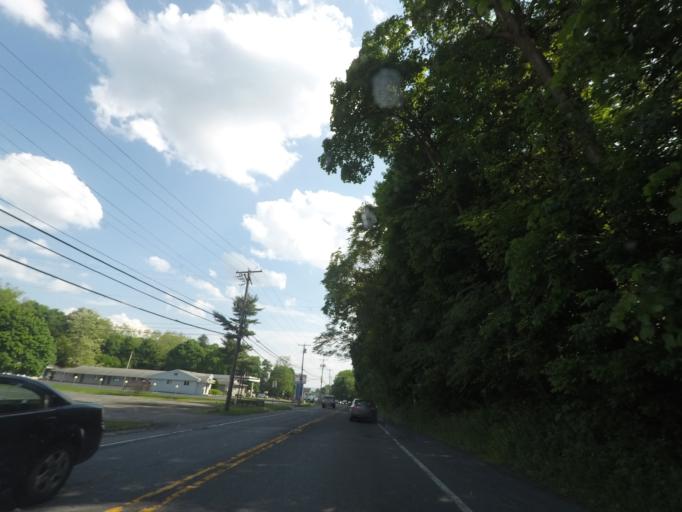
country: US
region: New York
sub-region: Orange County
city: Balmville
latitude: 41.5432
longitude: -74.0123
